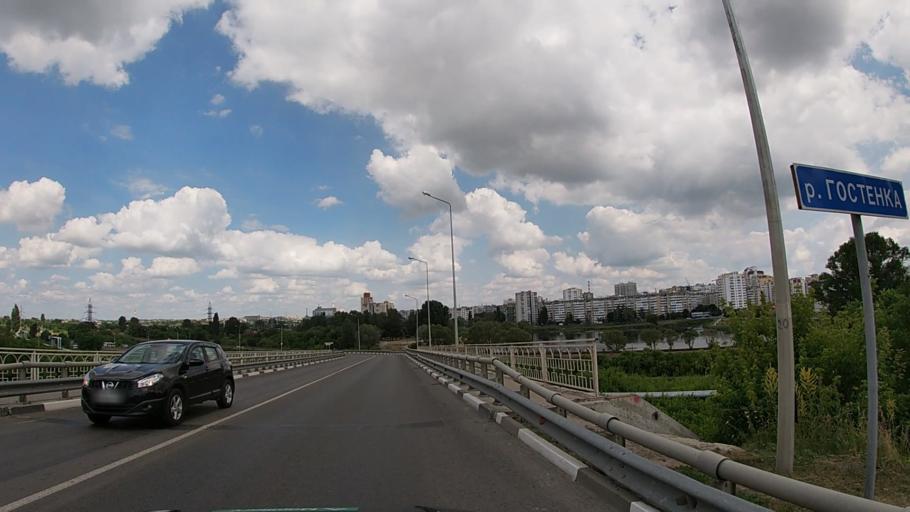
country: RU
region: Belgorod
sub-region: Belgorodskiy Rayon
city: Belgorod
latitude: 50.5900
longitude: 36.5660
